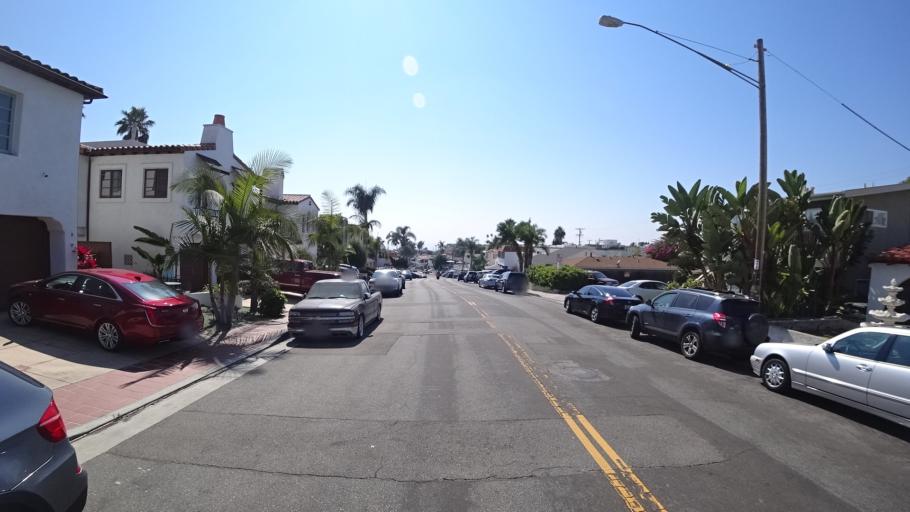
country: US
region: California
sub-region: Orange County
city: San Clemente
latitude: 33.4245
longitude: -117.6158
